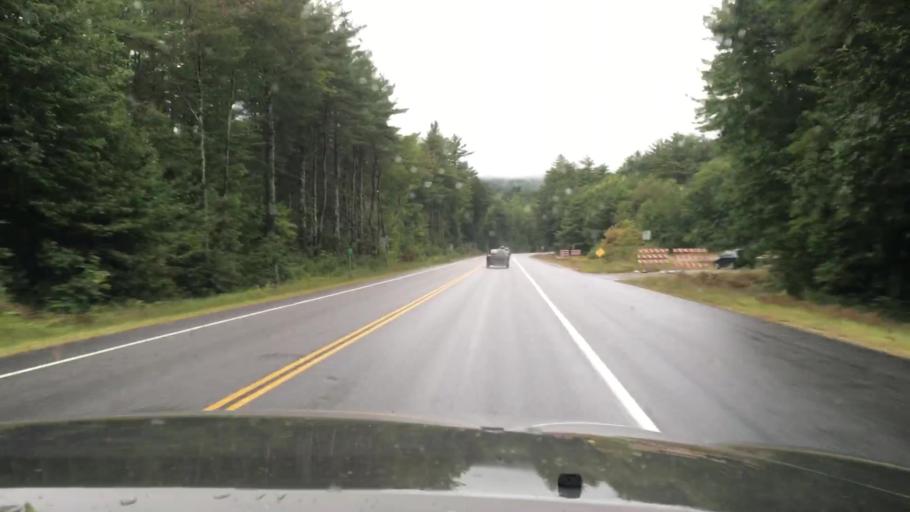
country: US
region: New Hampshire
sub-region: Hillsborough County
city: Antrim
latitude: 43.0686
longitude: -72.0325
